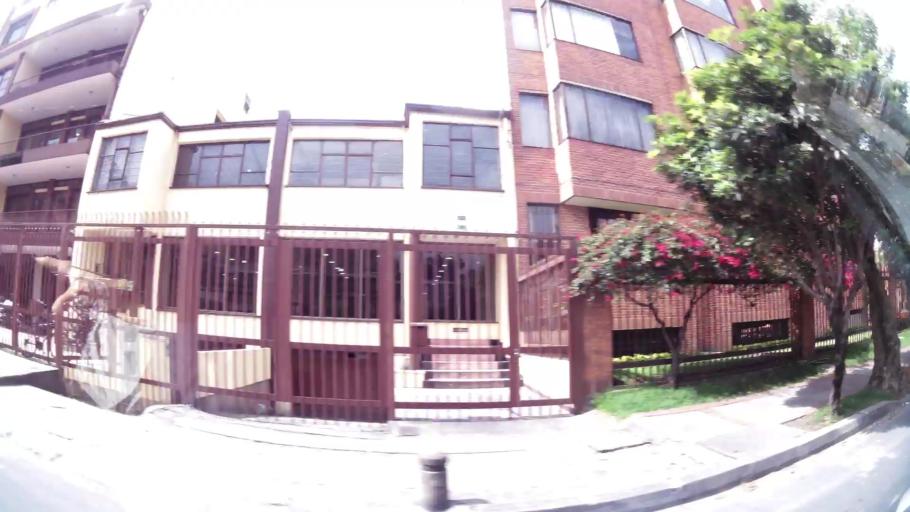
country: CO
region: Bogota D.C.
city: Bogota
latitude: 4.6267
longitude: -74.0761
